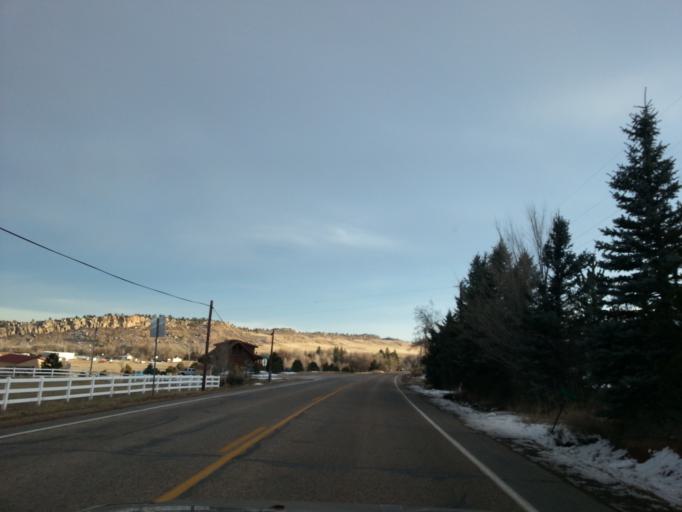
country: US
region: Colorado
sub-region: Larimer County
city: Loveland
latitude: 40.4226
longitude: -105.1908
